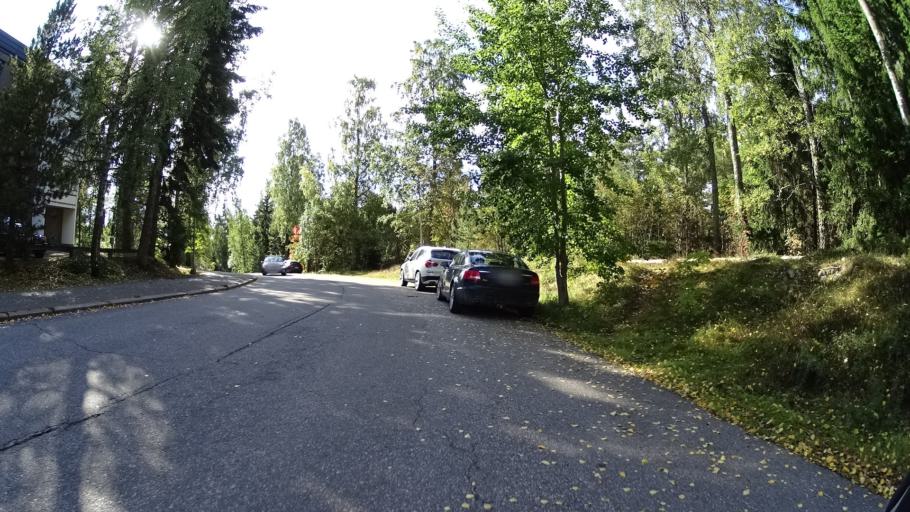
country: FI
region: Uusimaa
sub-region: Helsinki
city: Teekkarikylae
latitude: 60.1785
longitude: 24.8527
